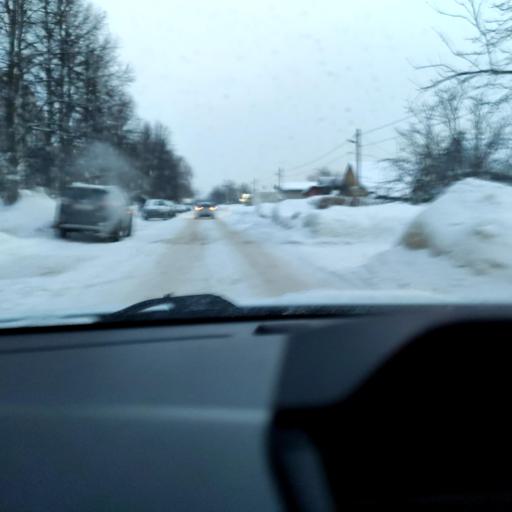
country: RU
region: Tatarstan
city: Vysokaya Gora
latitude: 55.8731
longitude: 49.2380
